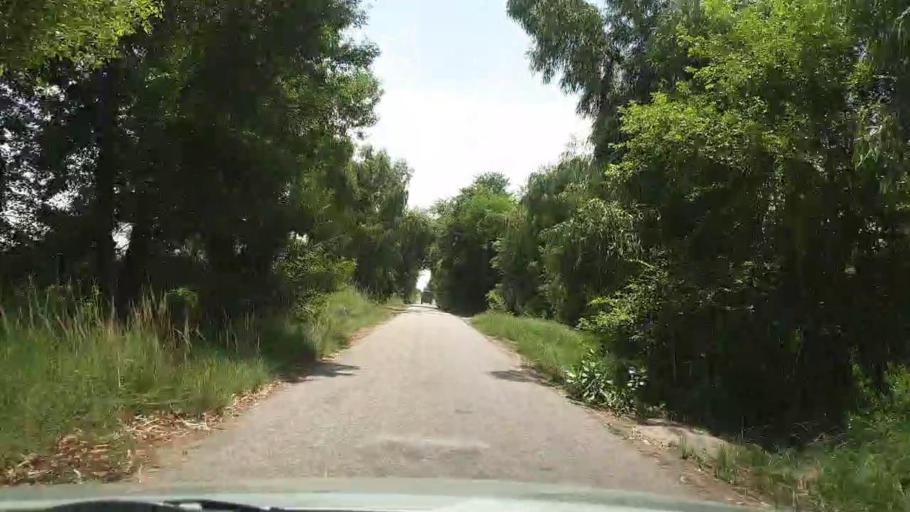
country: PK
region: Sindh
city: Bozdar
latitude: 27.0728
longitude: 68.9749
